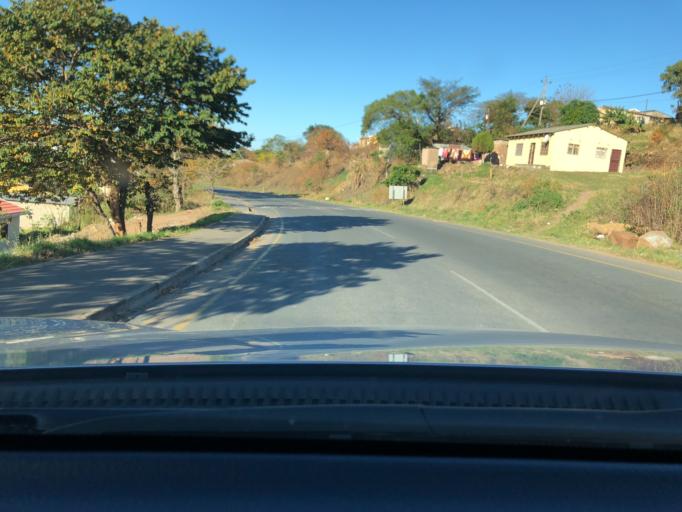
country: ZA
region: KwaZulu-Natal
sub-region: eThekwini Metropolitan Municipality
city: Umkomaas
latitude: -30.0372
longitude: 30.8539
